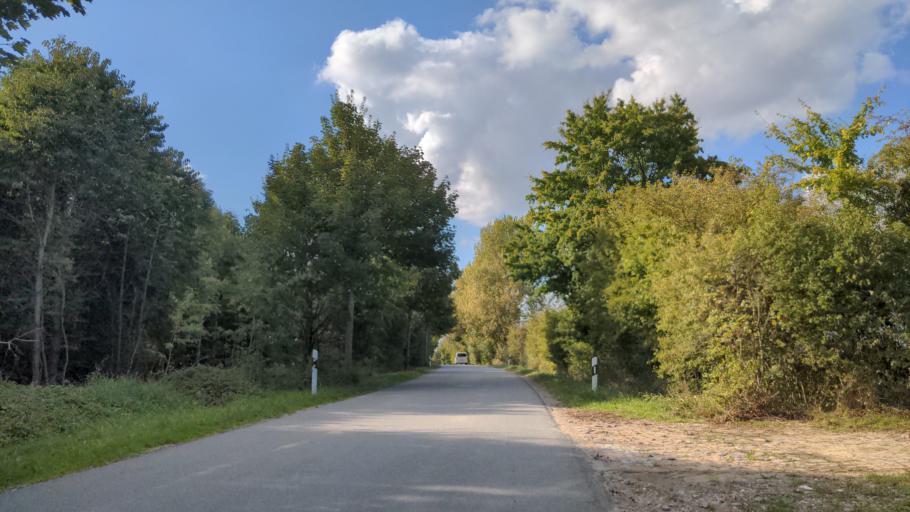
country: DE
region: Schleswig-Holstein
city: Monkhagen
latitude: 53.9208
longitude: 10.5836
